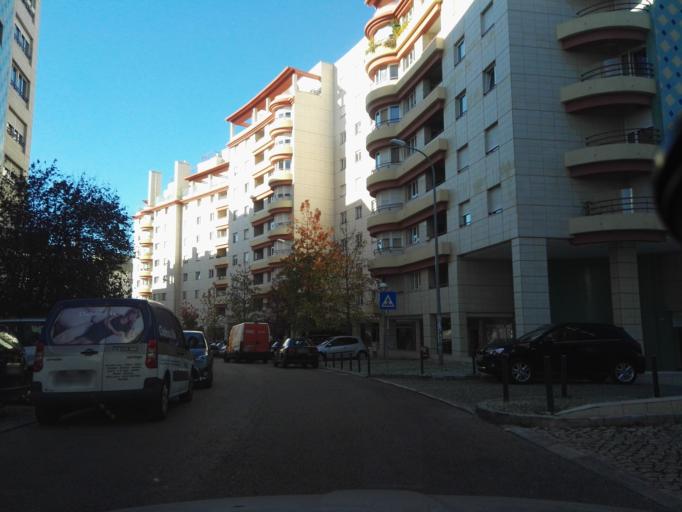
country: PT
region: Lisbon
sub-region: Odivelas
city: Olival do Basto
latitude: 38.7678
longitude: -9.1530
